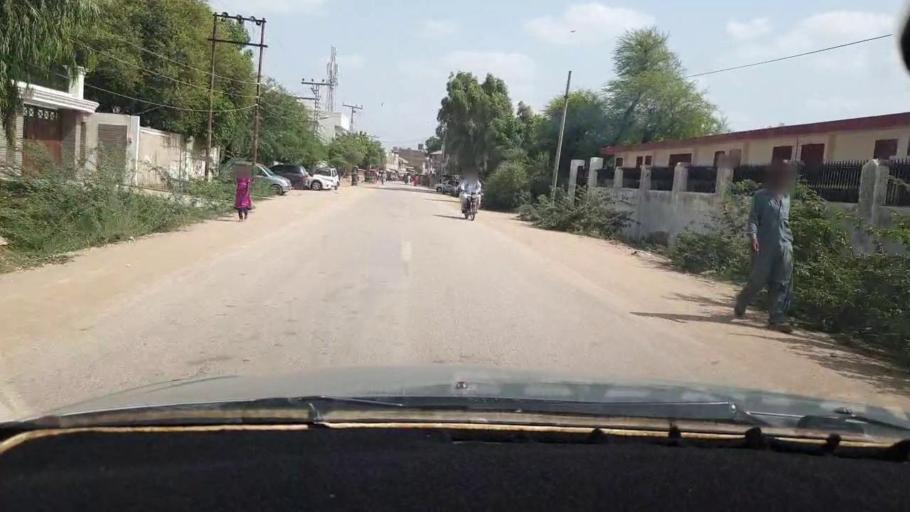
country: PK
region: Sindh
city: Digri
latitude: 25.0744
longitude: 69.2138
